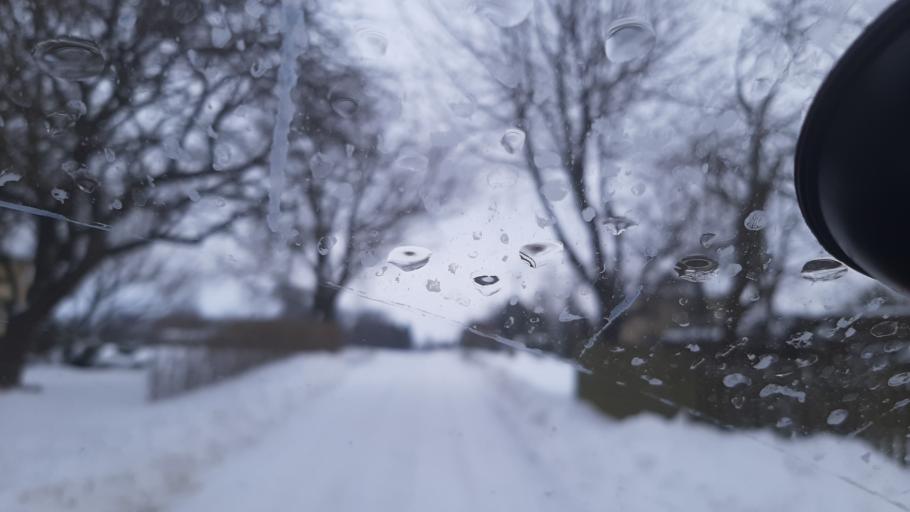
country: PL
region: Lublin Voivodeship
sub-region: Powiat lubelski
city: Jastkow
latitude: 51.3495
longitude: 22.3934
